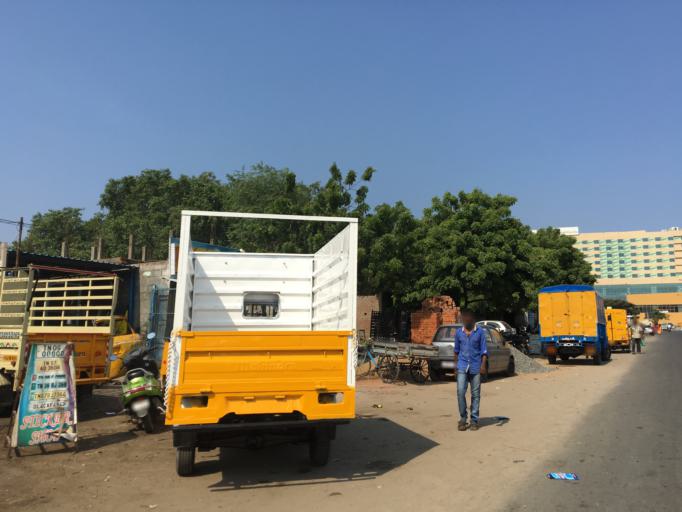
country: IN
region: Tamil Nadu
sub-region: Kancheepuram
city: Perungudi
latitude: 12.9806
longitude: 80.2503
